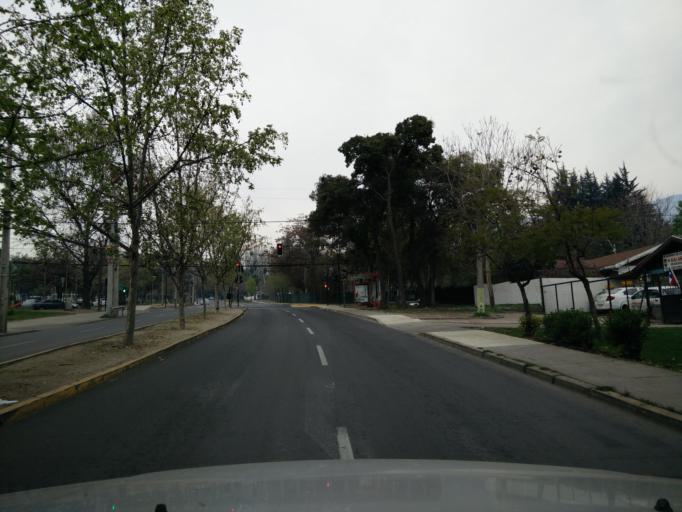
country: CL
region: Santiago Metropolitan
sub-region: Provincia de Santiago
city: Villa Presidente Frei, Nunoa, Santiago, Chile
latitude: -33.4052
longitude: -70.5390
